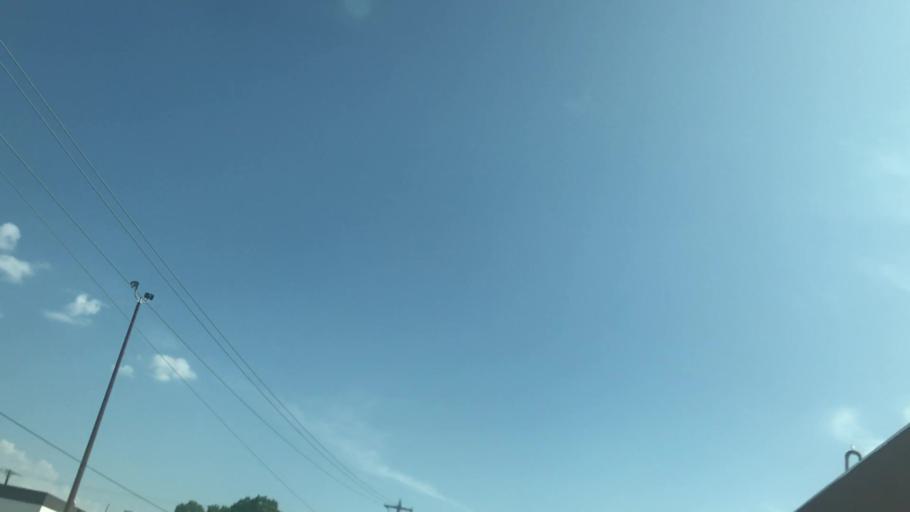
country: US
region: Wisconsin
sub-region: Brown County
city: Allouez
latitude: 44.4918
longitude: -88.0382
